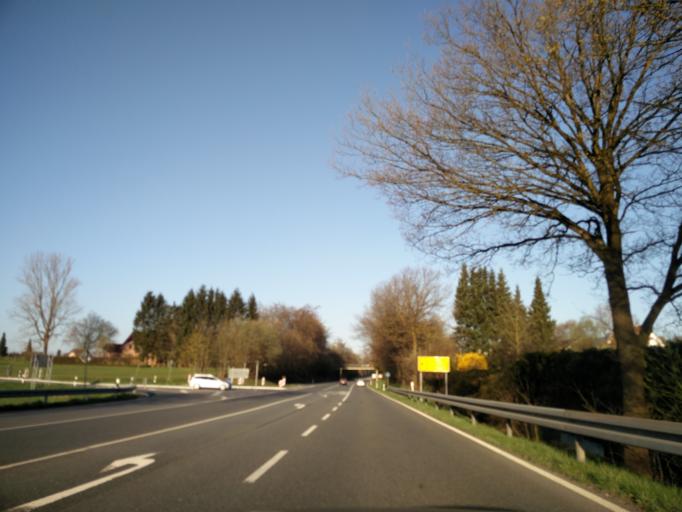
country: DE
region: North Rhine-Westphalia
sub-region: Regierungsbezirk Detmold
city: Altenbeken
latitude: 51.7394
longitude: 8.9529
